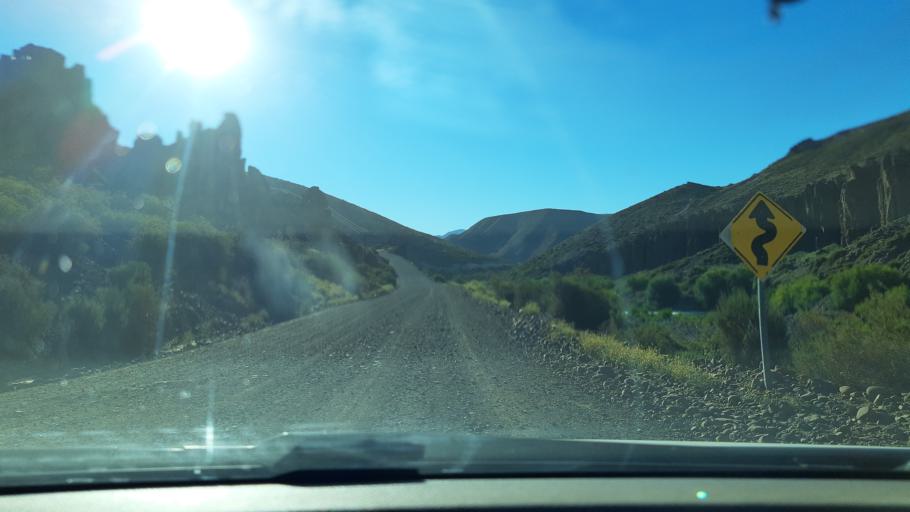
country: AR
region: Neuquen
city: Las Ovejas
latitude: -36.8086
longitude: -70.7153
